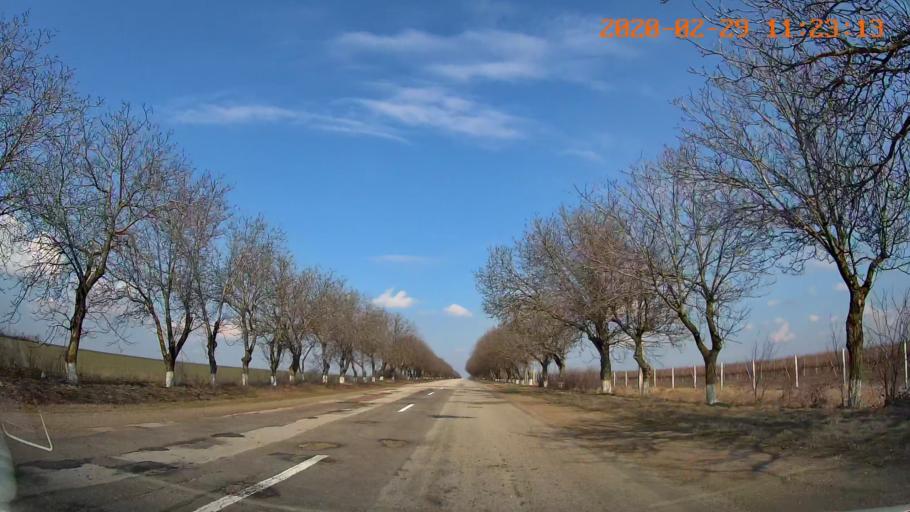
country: MD
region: Telenesti
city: Cocieri
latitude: 47.4049
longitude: 29.1598
